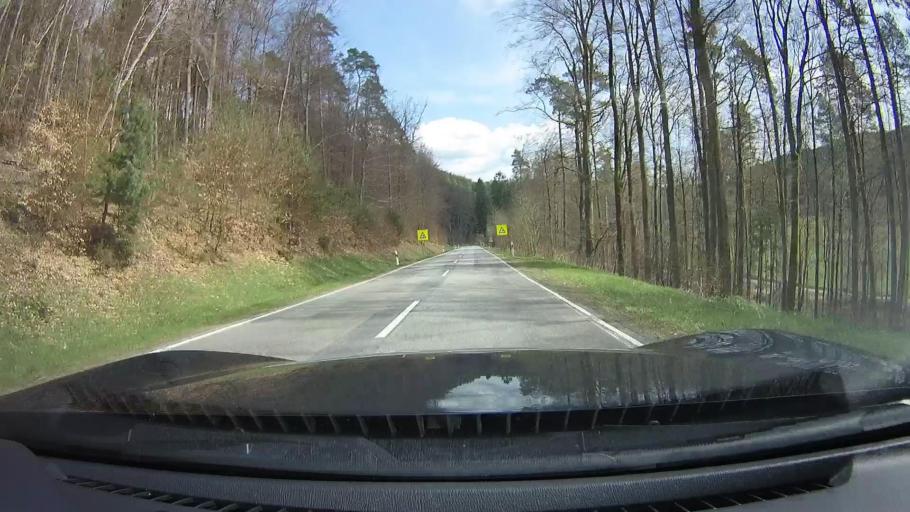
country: DE
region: Hesse
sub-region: Regierungsbezirk Darmstadt
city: Hesseneck
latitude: 49.5790
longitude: 9.0422
